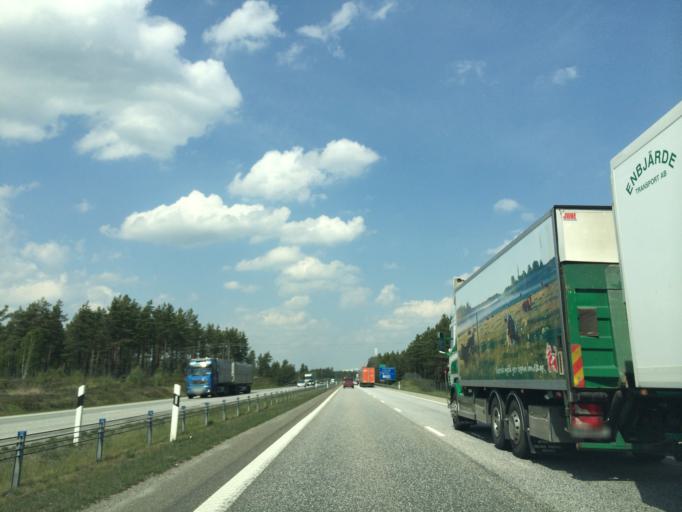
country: SE
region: Joenkoeping
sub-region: Jonkopings Kommun
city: Odensjo
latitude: 57.6796
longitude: 14.1669
